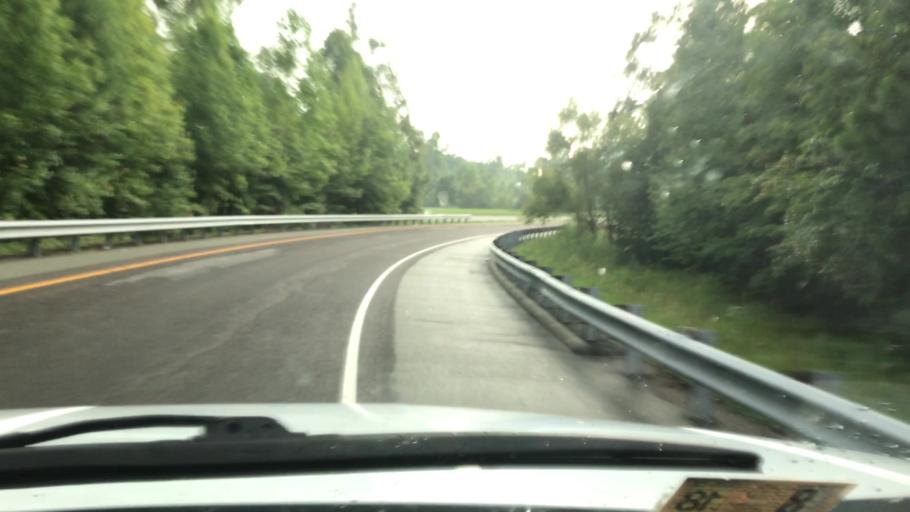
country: US
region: Virginia
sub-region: Henrico County
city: Short Pump
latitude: 37.6342
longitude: -77.6677
